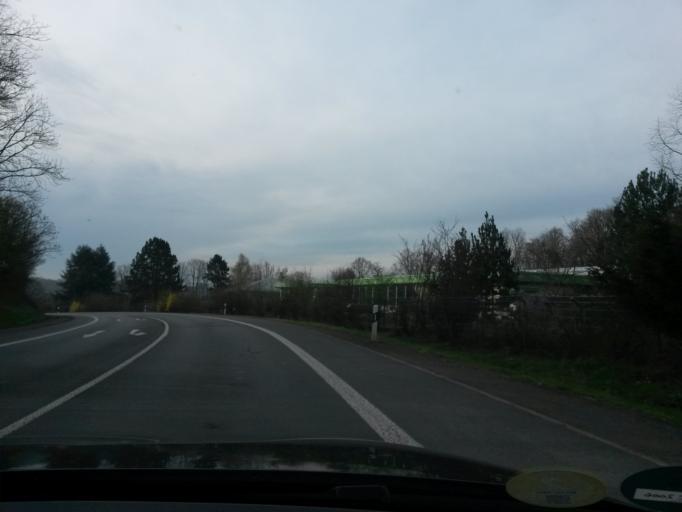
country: DE
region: North Rhine-Westphalia
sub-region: Regierungsbezirk Arnsberg
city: Luedenscheid
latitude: 51.2434
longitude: 7.5967
